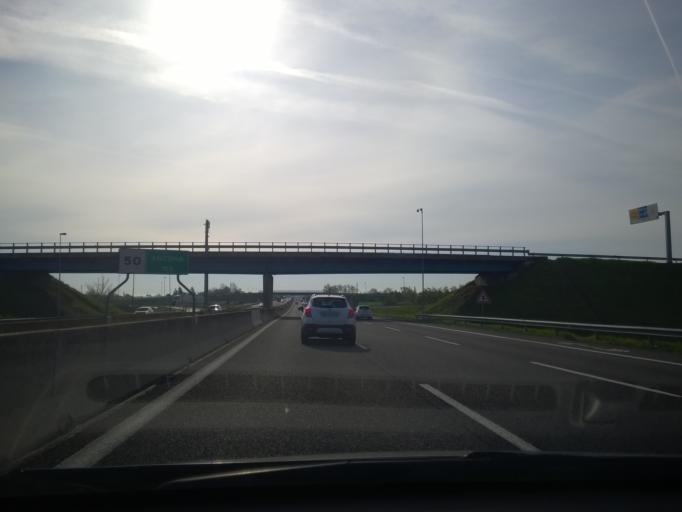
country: IT
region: Emilia-Romagna
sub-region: Provincia di Bologna
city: Imola
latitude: 44.3806
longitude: 11.7423
